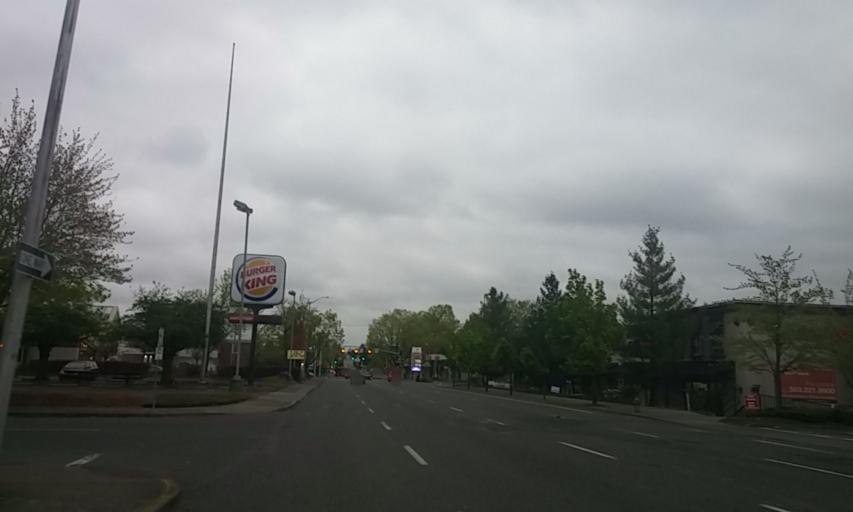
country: US
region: Oregon
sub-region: Multnomah County
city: Lents
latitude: 45.5184
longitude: -122.5606
